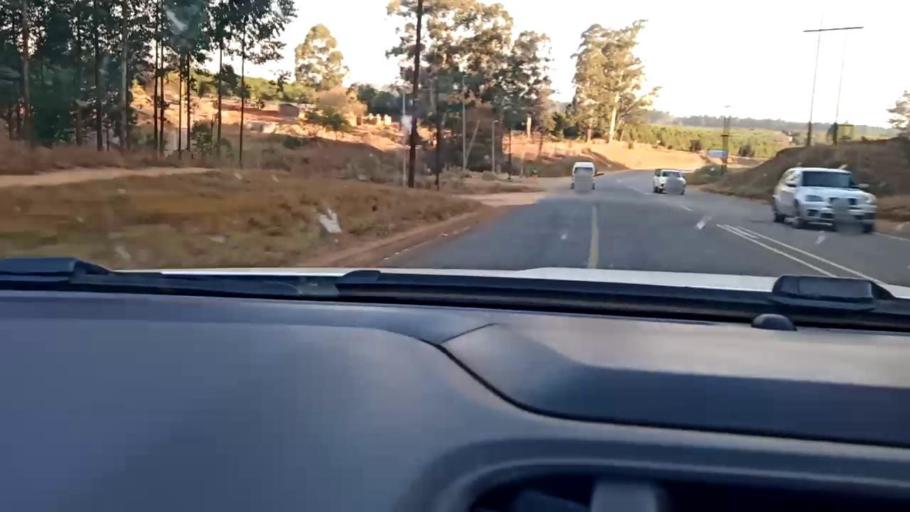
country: ZA
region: Limpopo
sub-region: Mopani District Municipality
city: Duiwelskloof
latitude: -23.7089
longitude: 30.1301
